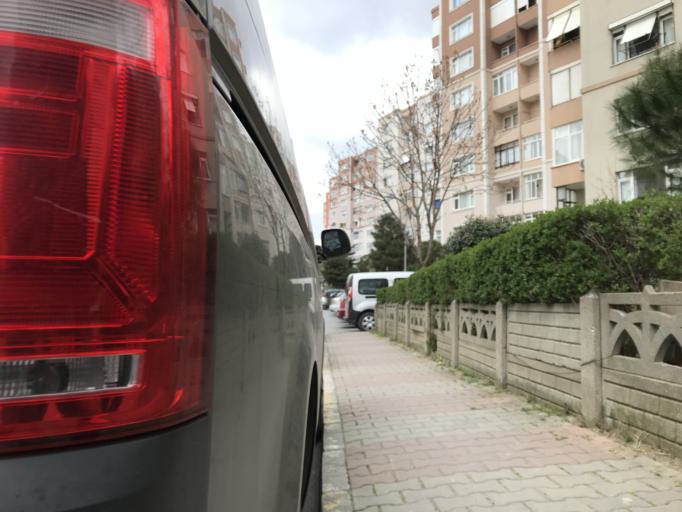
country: TR
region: Istanbul
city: Maltepe
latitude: 40.9403
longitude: 29.1366
